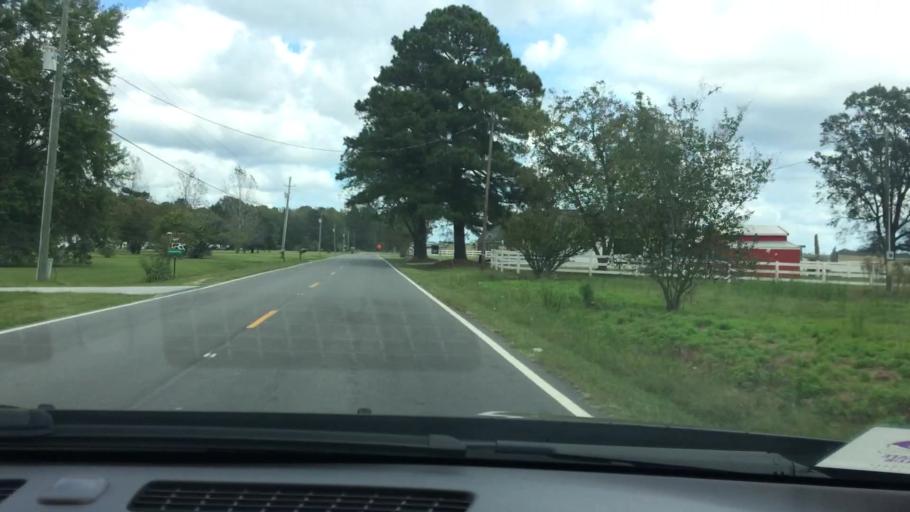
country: US
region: North Carolina
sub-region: Pitt County
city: Ayden
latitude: 35.4664
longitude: -77.4498
